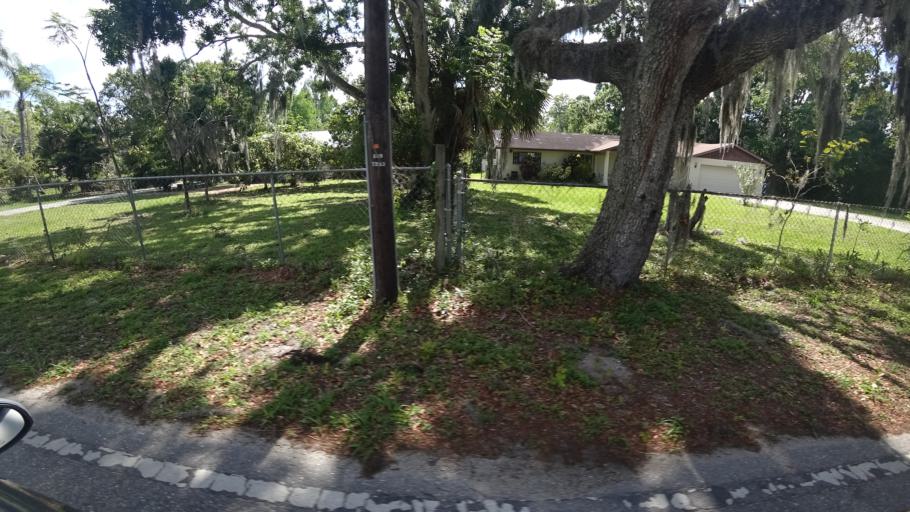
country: US
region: Florida
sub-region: Manatee County
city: Whitfield
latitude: 27.4123
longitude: -82.5289
